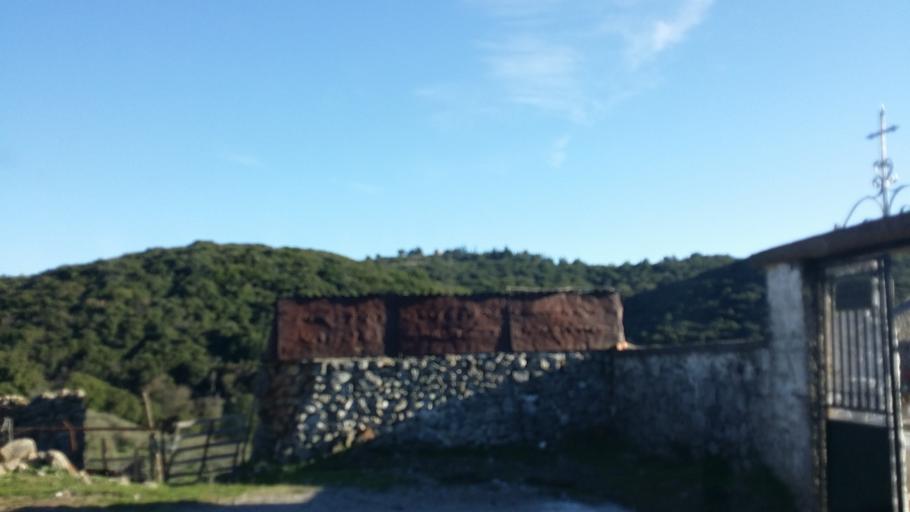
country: GR
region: West Greece
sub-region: Nomos Aitolias kai Akarnanias
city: Fitiai
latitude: 38.7050
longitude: 21.1779
